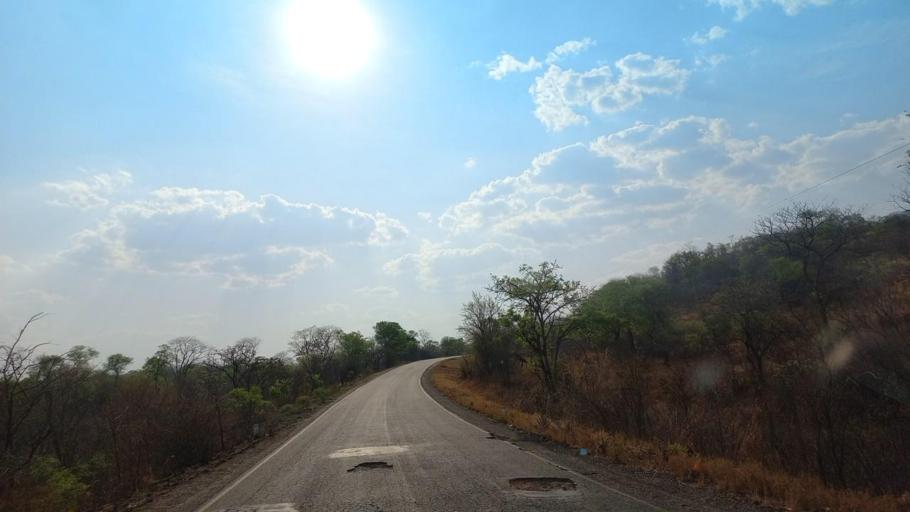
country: ZM
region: Lusaka
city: Luangwa
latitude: -14.9837
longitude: 30.1586
